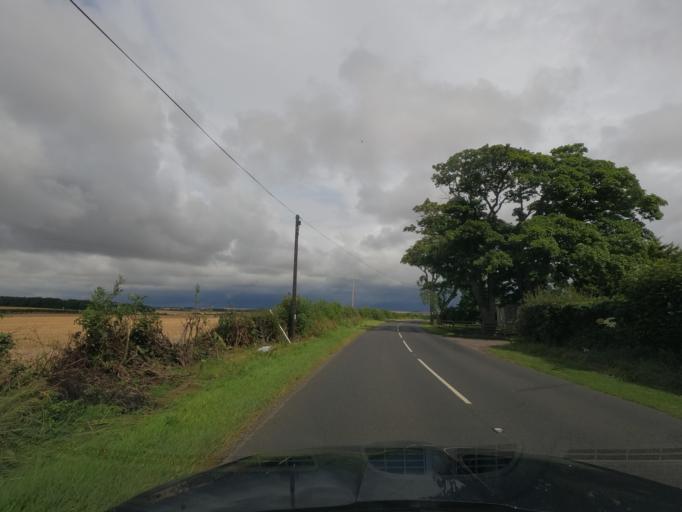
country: GB
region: England
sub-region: Northumberland
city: Ancroft
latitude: 55.6860
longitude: -2.0023
